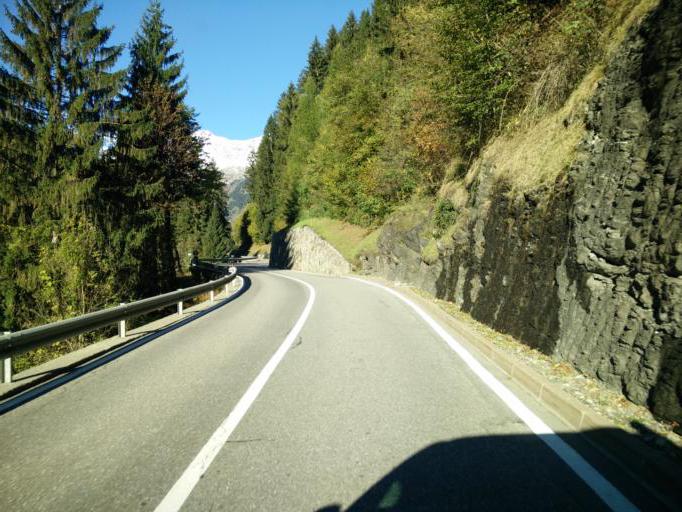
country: IT
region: Trentino-Alto Adige
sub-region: Bolzano
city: Moso in Passiria
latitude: 46.8222
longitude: 11.2003
